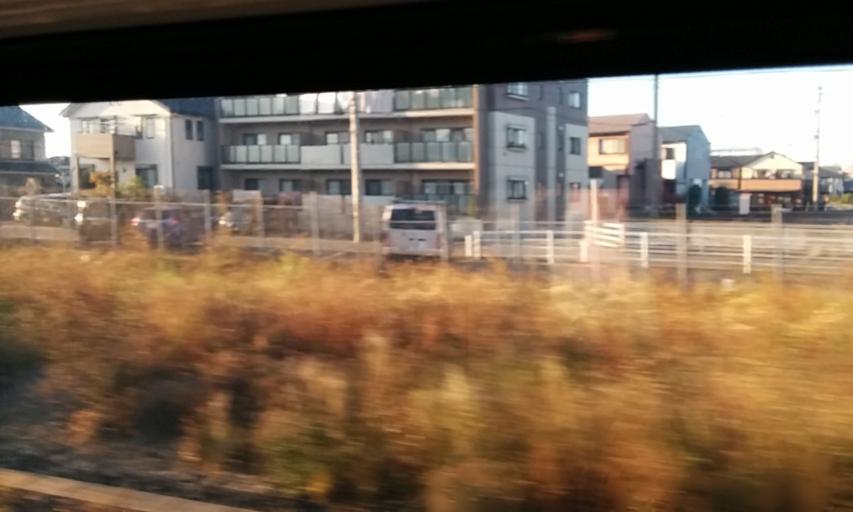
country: JP
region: Aichi
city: Kasugai
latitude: 35.2600
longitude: 137.0166
